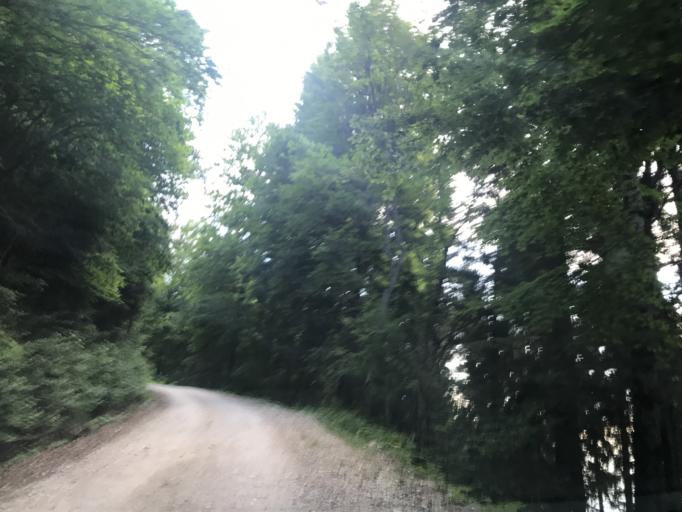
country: FR
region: Rhone-Alpes
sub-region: Departement de l'Isere
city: Saint-Vincent-de-Mercuze
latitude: 45.4104
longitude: 5.9354
